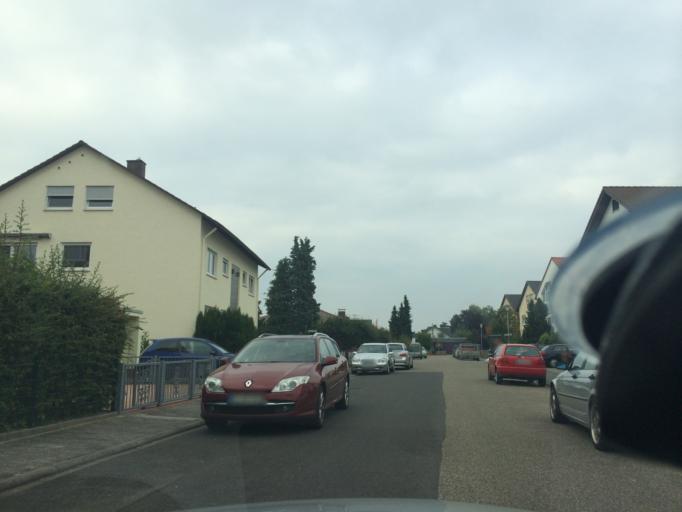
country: DE
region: Hesse
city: Morfelden-Walldorf
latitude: 49.9979
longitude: 8.5687
